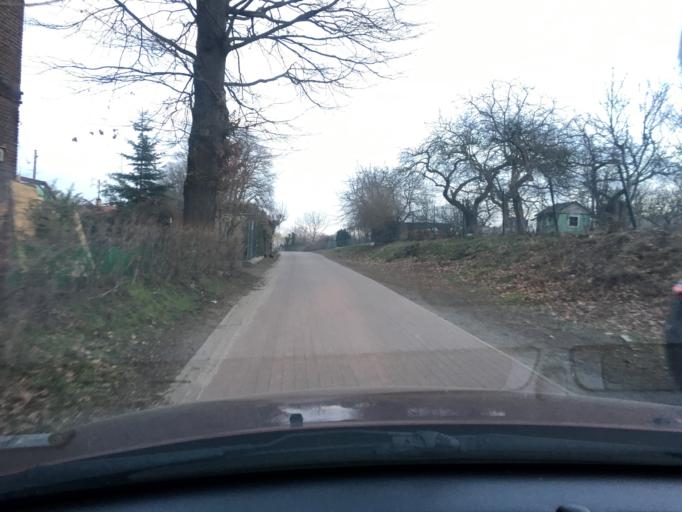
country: PL
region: Lower Silesian Voivodeship
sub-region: Powiat zgorzelecki
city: Zgorzelec
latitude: 51.1403
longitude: 14.9967
